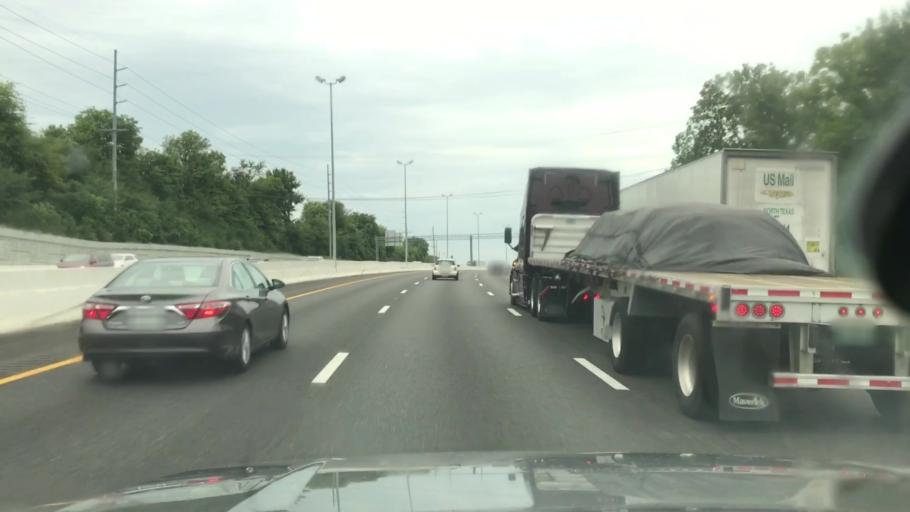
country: US
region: Tennessee
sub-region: Davidson County
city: Lakewood
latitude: 36.1944
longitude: -86.6875
